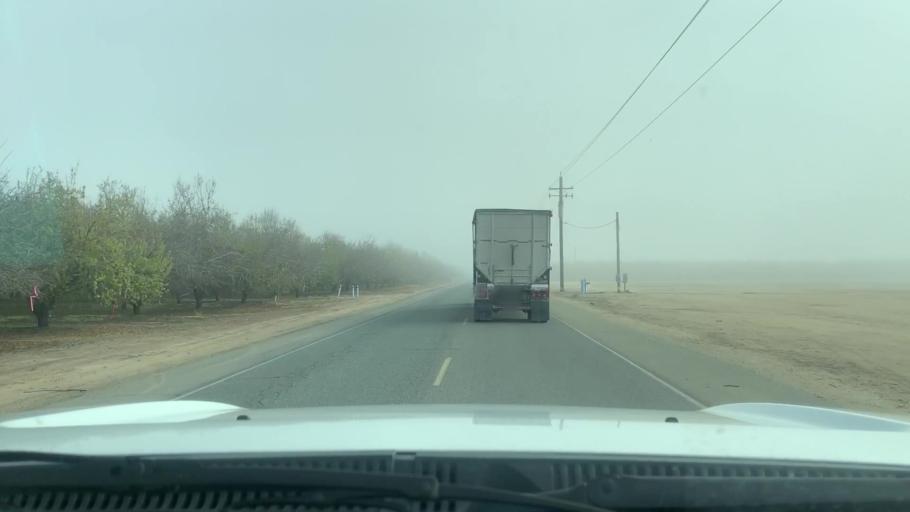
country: US
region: California
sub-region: Kern County
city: Buttonwillow
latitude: 35.5008
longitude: -119.5216
